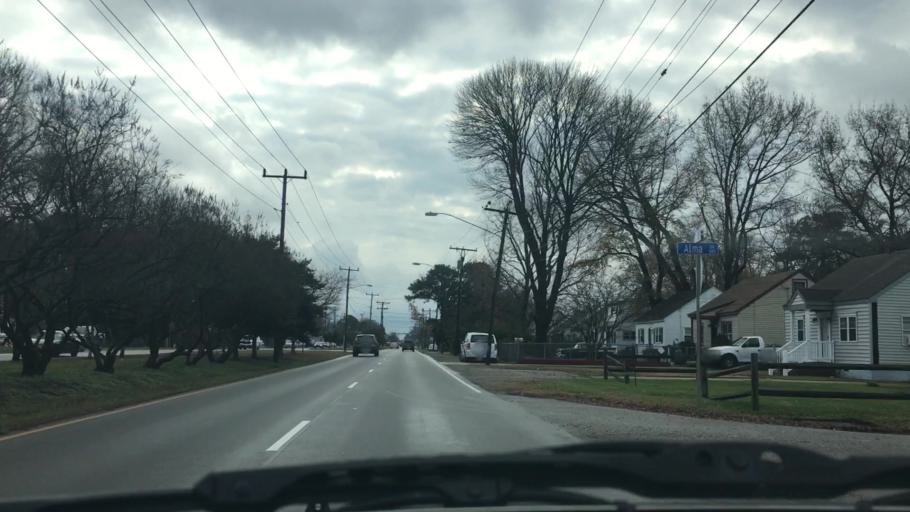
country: US
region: Virginia
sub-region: City of Norfolk
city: Norfolk
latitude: 36.9189
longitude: -76.2423
